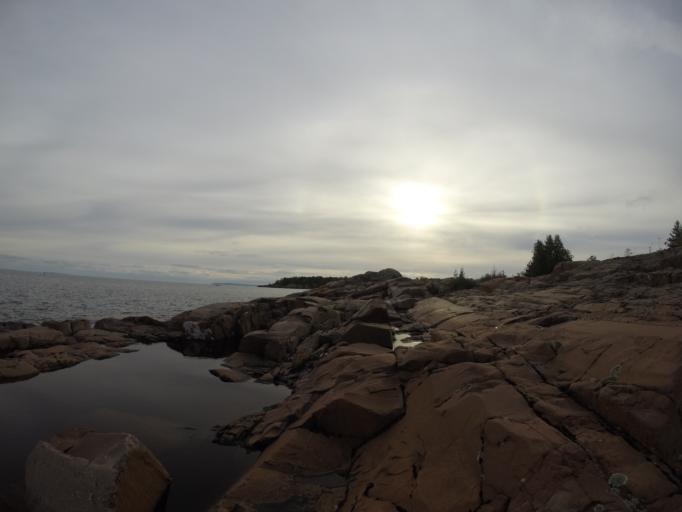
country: CA
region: Ontario
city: Espanola
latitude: 45.9687
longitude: -81.4937
